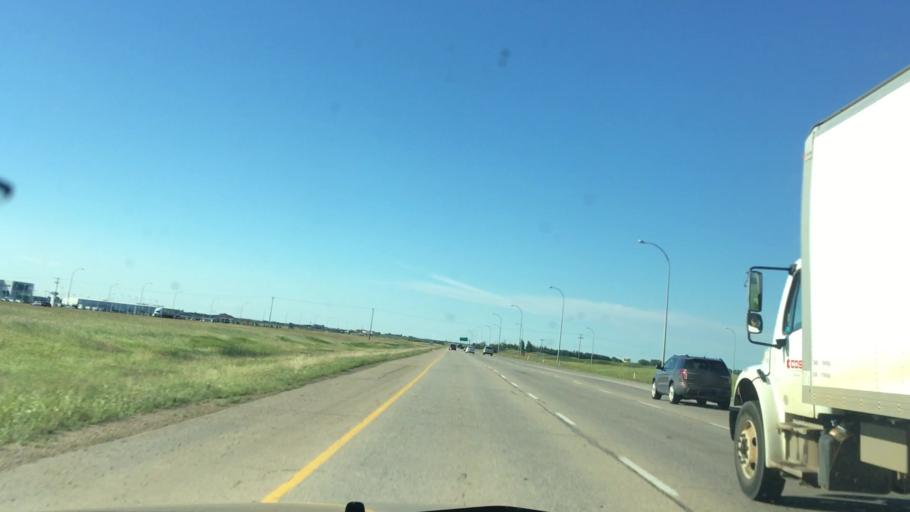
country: CA
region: Alberta
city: Leduc
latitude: 53.3366
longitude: -113.5493
